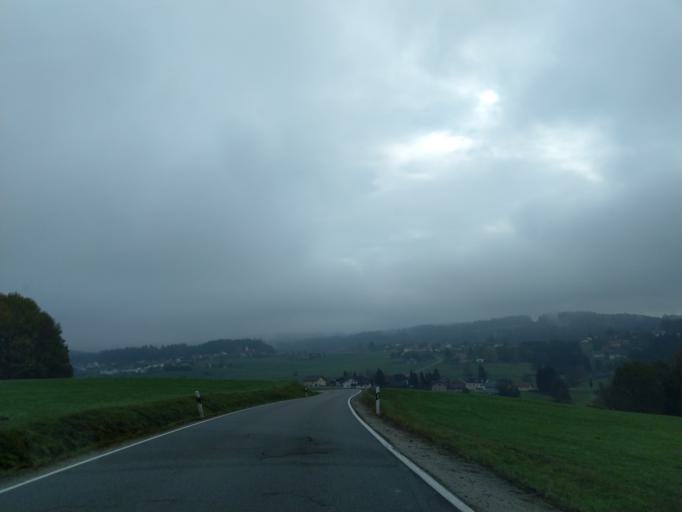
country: DE
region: Bavaria
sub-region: Lower Bavaria
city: Auerbach
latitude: 48.7896
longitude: 13.1090
